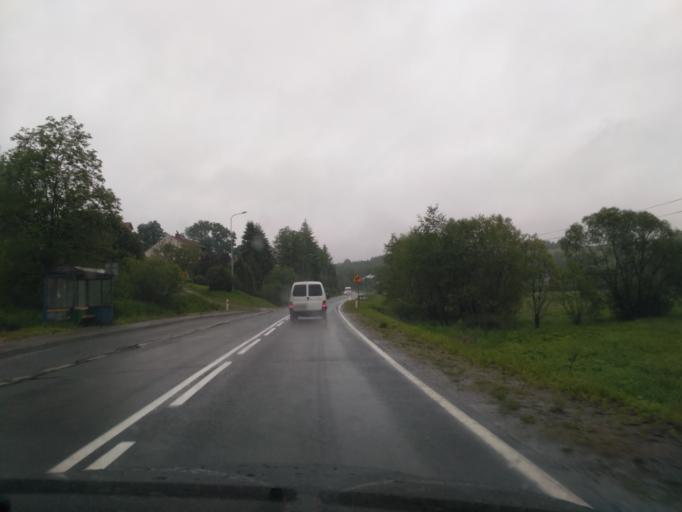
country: PL
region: Subcarpathian Voivodeship
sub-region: Powiat strzyzowski
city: Frysztak
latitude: 49.8141
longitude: 21.6202
